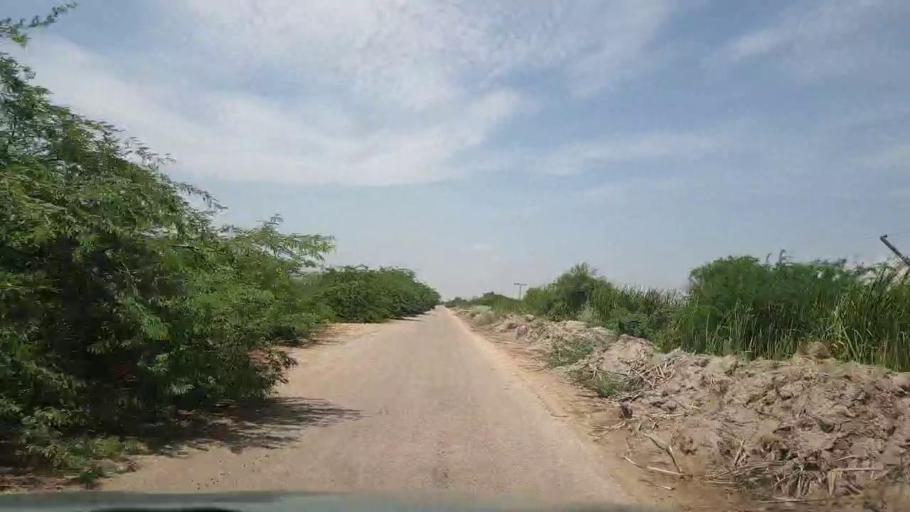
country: PK
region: Sindh
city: Bozdar
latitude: 27.0861
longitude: 68.9872
